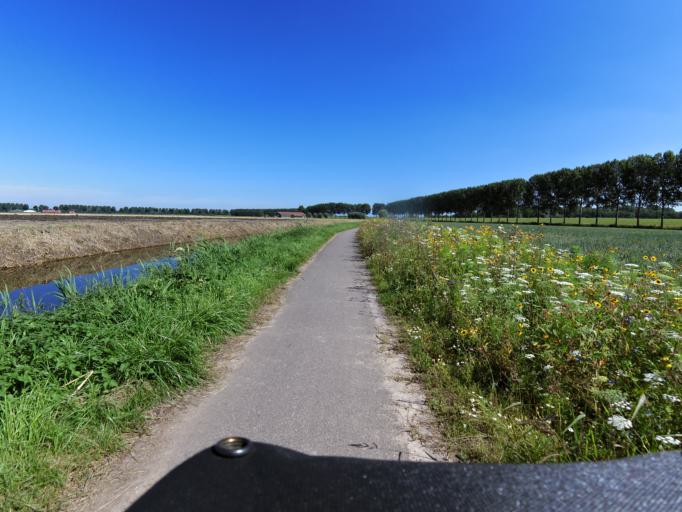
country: NL
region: South Holland
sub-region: Gemeente Dordrecht
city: Dordrecht
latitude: 51.7526
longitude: 4.7069
